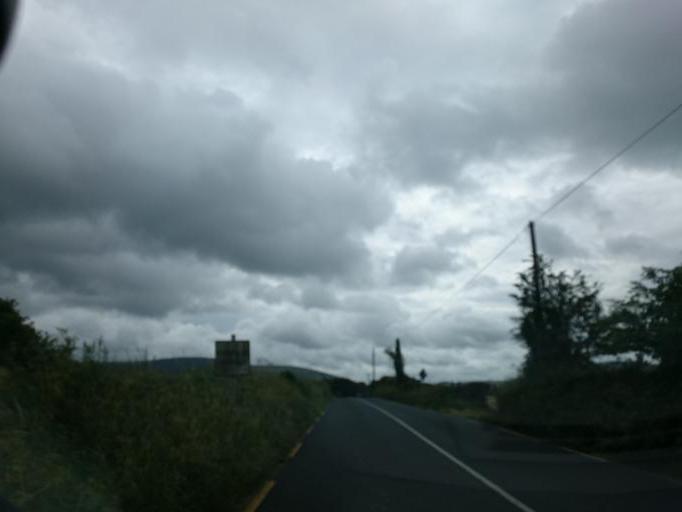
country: IE
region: Leinster
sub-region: Wicklow
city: Carnew
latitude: 52.8365
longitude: -6.5336
